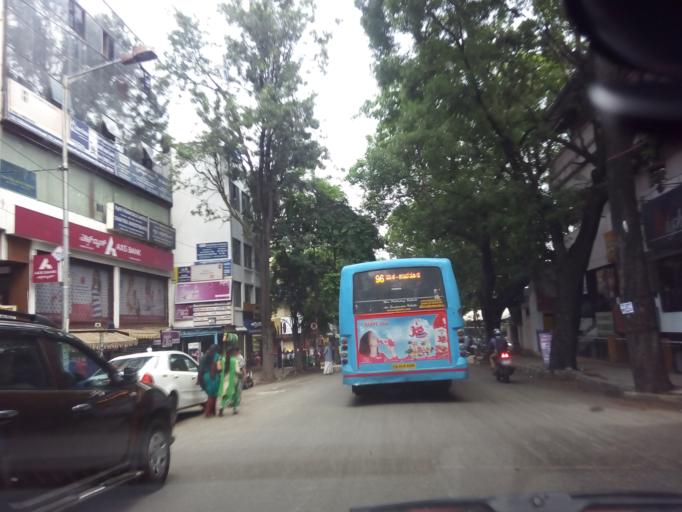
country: IN
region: Karnataka
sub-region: Bangalore Urban
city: Bangalore
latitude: 12.9988
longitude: 77.5694
